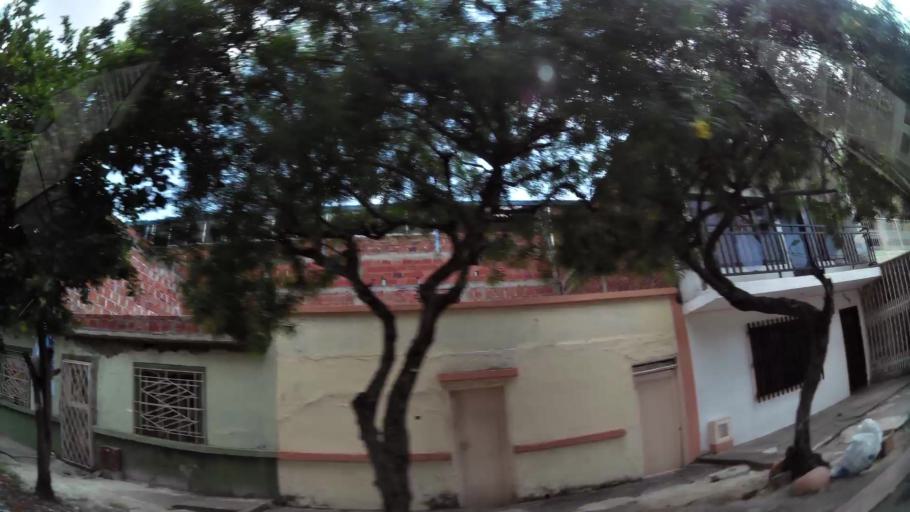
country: CO
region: Valle del Cauca
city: Cali
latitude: 3.4186
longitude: -76.5199
